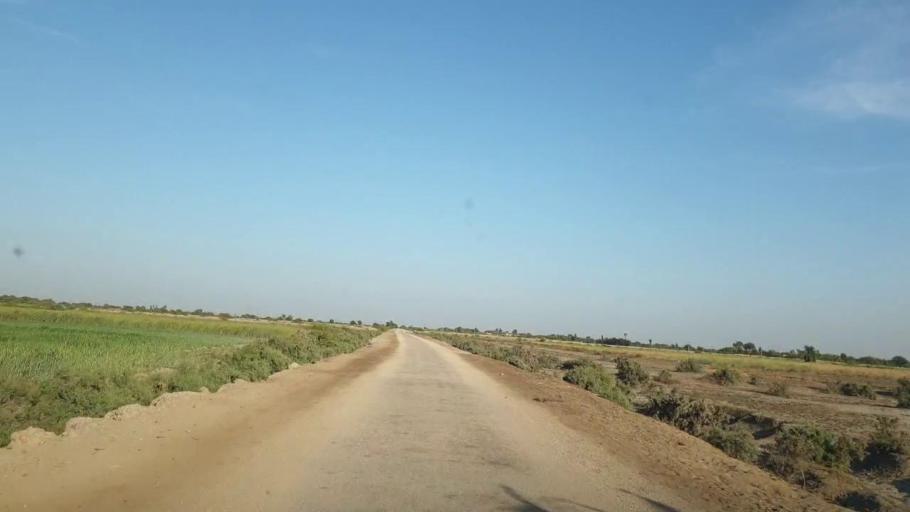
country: PK
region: Sindh
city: Kunri
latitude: 25.0912
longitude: 69.4122
